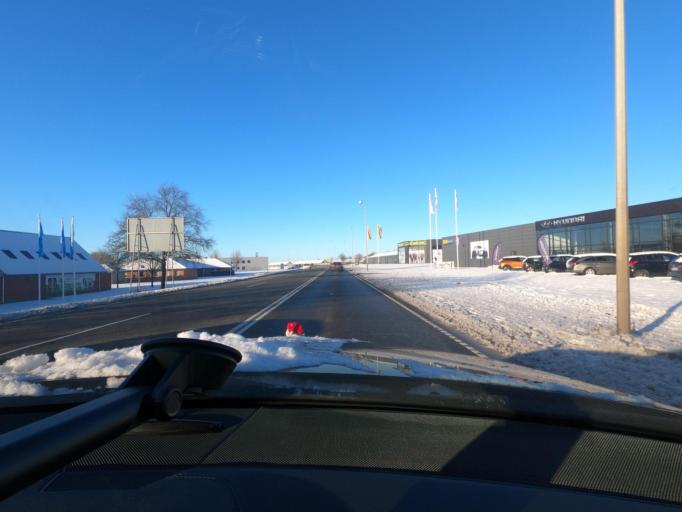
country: DK
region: South Denmark
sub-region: Aabenraa Kommune
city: Rodekro
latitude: 55.0682
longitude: 9.3590
